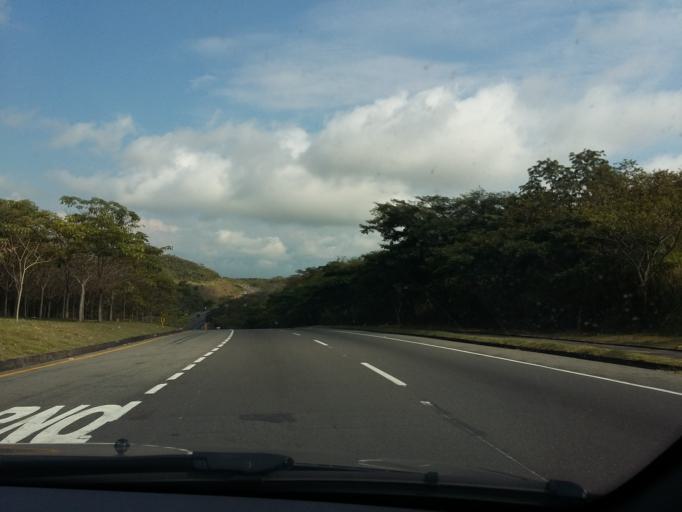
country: CO
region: Tolima
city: Valle de San Juan
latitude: 4.3479
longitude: -75.1054
